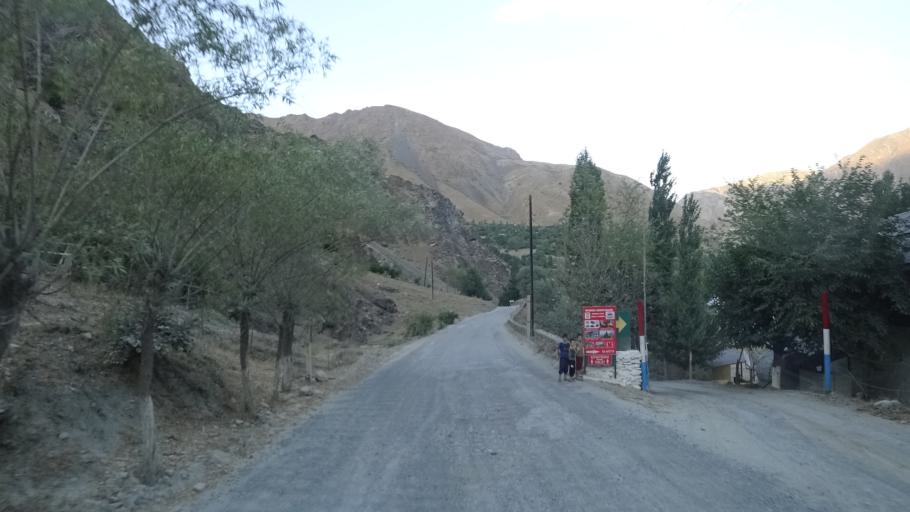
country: AF
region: Badakhshan
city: Nusay
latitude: 38.4548
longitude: 70.8248
